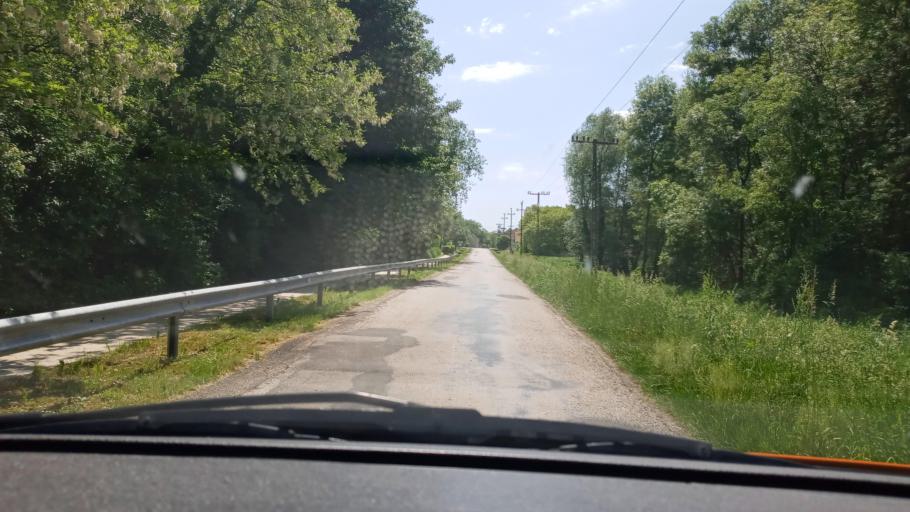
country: HU
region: Baranya
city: Harkany
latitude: 45.8377
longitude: 18.2046
